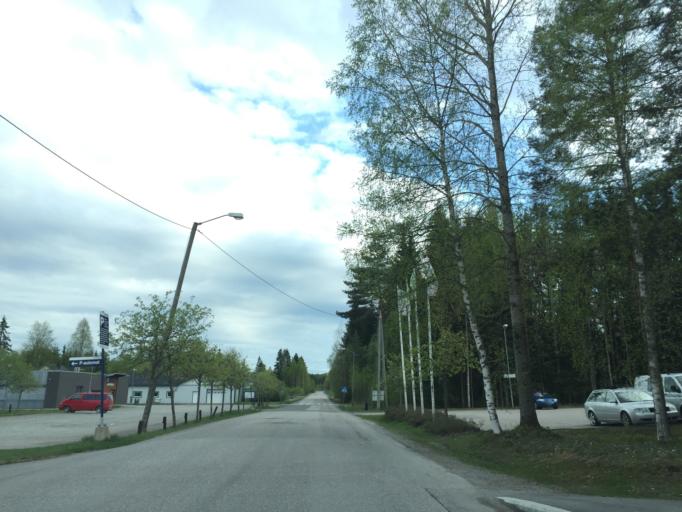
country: NO
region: Hedmark
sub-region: Kongsvinger
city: Kongsvinger
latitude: 60.1737
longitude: 12.0174
